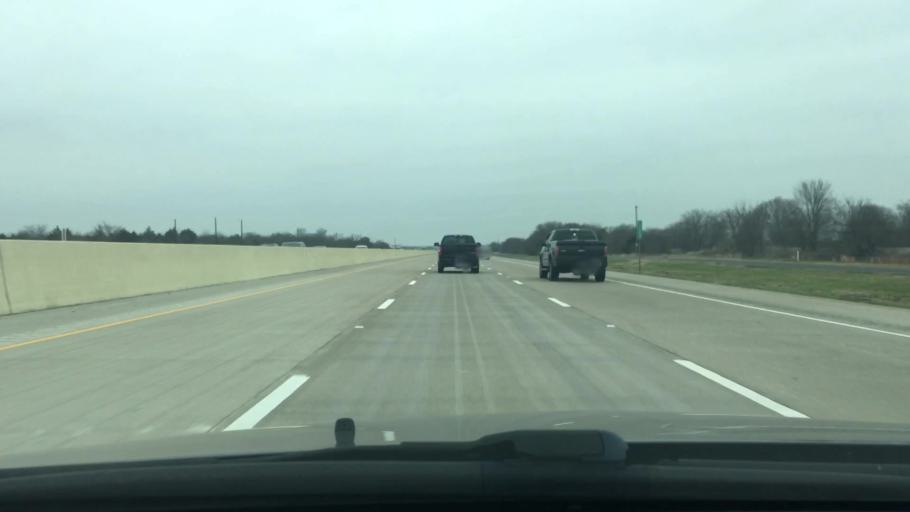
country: US
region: Texas
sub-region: Navarro County
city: Corsicana
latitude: 31.9814
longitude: -96.4238
